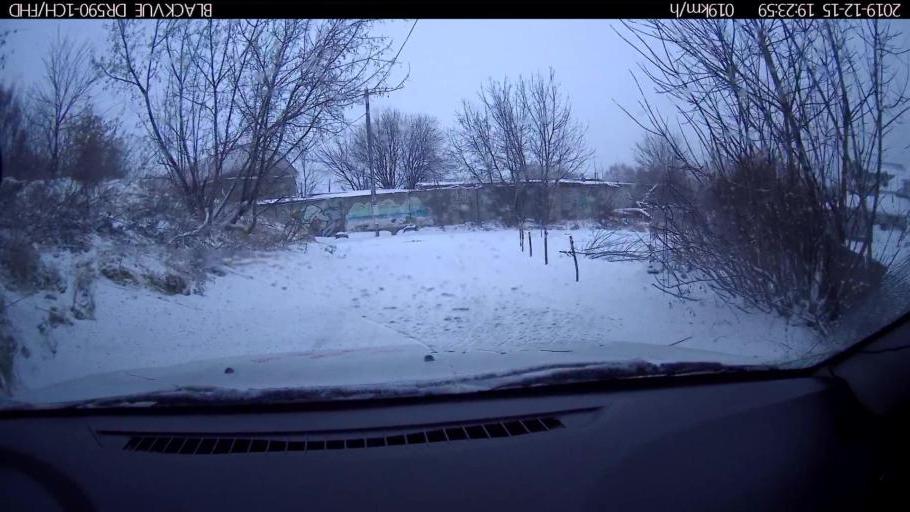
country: RU
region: Nizjnij Novgorod
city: Afonino
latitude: 56.3089
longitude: 44.0840
